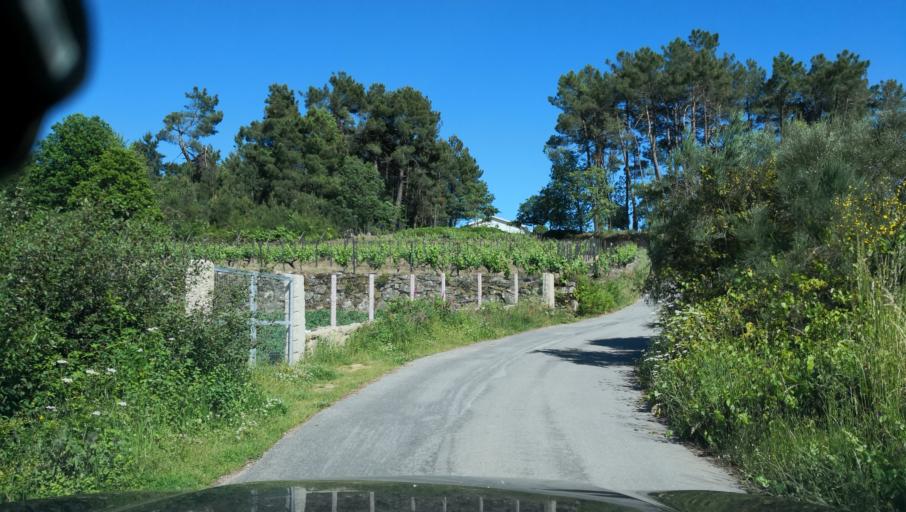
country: PT
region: Vila Real
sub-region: Vila Real
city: Vila Real
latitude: 41.3010
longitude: -7.6629
